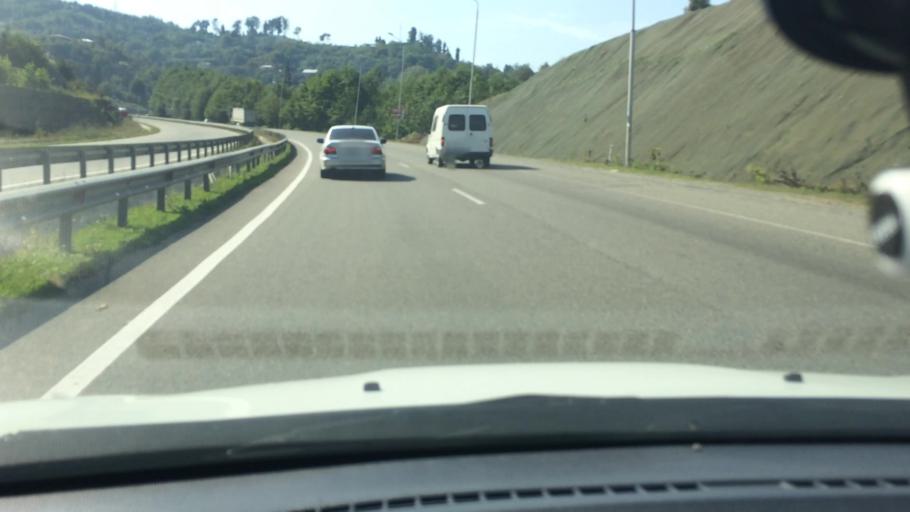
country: GE
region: Ajaria
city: Makhinjauri
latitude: 41.6993
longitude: 41.7288
